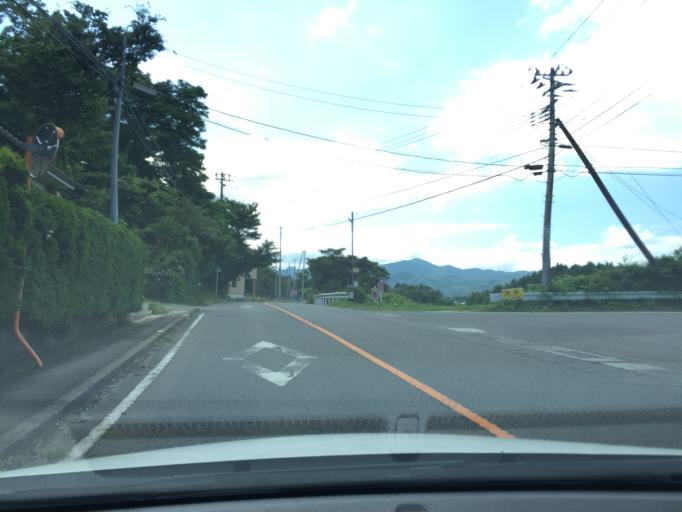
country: JP
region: Fukushima
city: Koriyama
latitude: 37.3644
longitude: 140.2975
